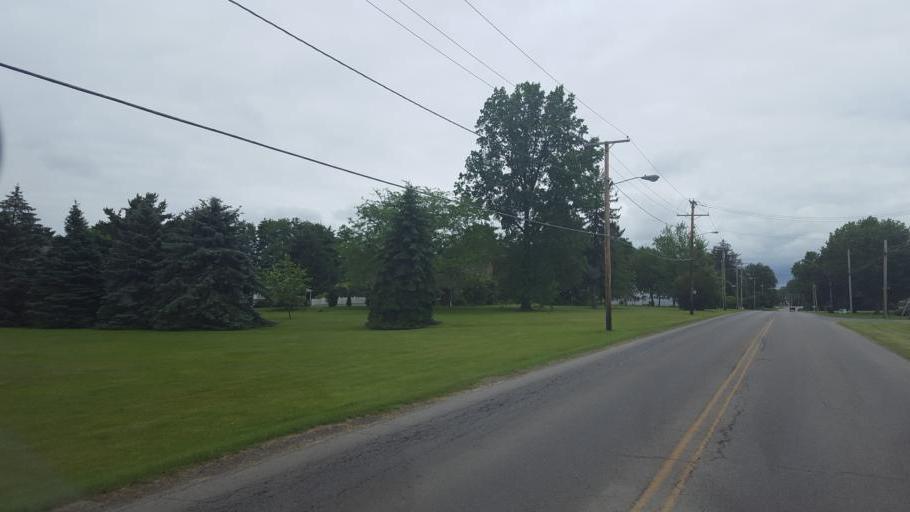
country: US
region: Ohio
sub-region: Crawford County
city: Galion
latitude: 40.7358
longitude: -82.8133
